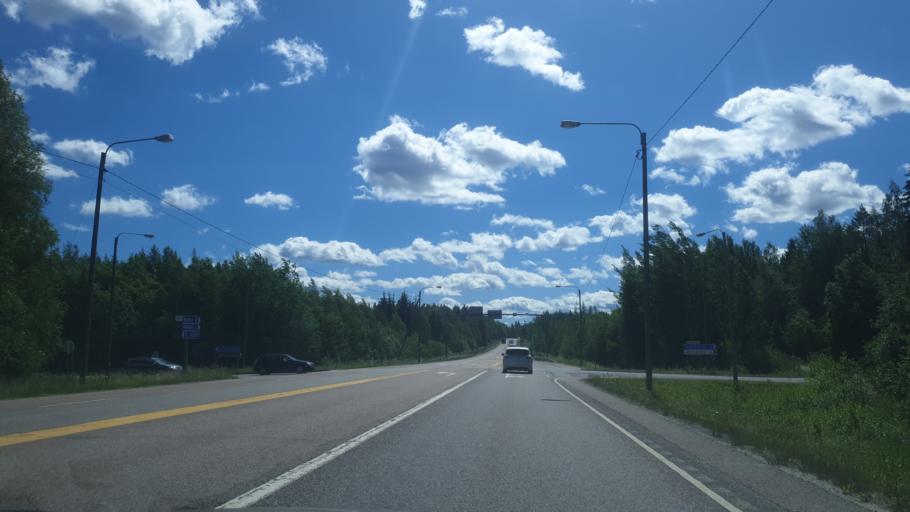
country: FI
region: Northern Savo
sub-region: Varkaus
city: Varkaus
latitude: 62.3521
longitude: 27.8166
